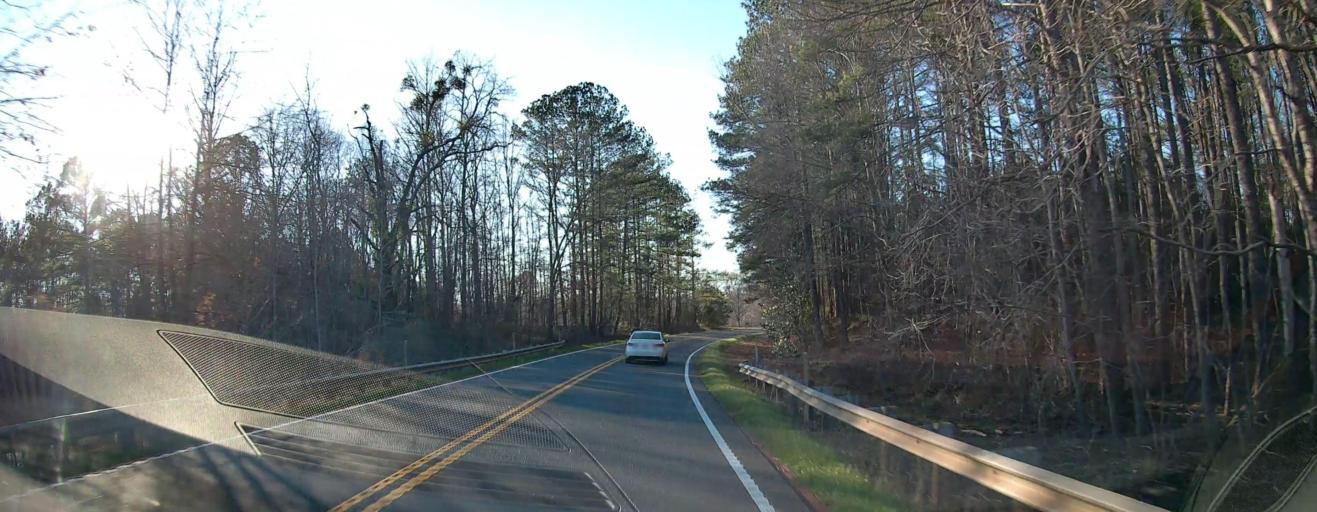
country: US
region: Georgia
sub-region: Harris County
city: Pine Mountain
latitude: 32.9153
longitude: -84.7606
